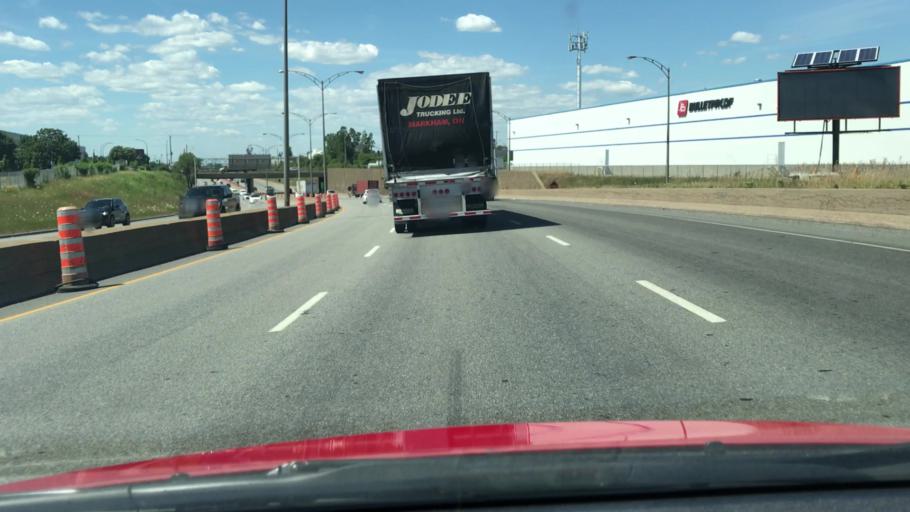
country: CA
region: Quebec
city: Cote-Saint-Luc
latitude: 45.4659
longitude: -73.6964
